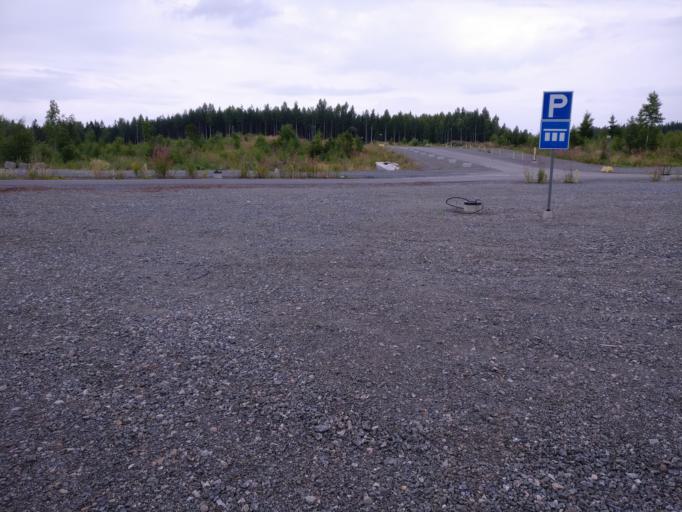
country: FI
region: Pirkanmaa
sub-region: Tampere
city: Tampere
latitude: 61.4396
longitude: 23.8078
